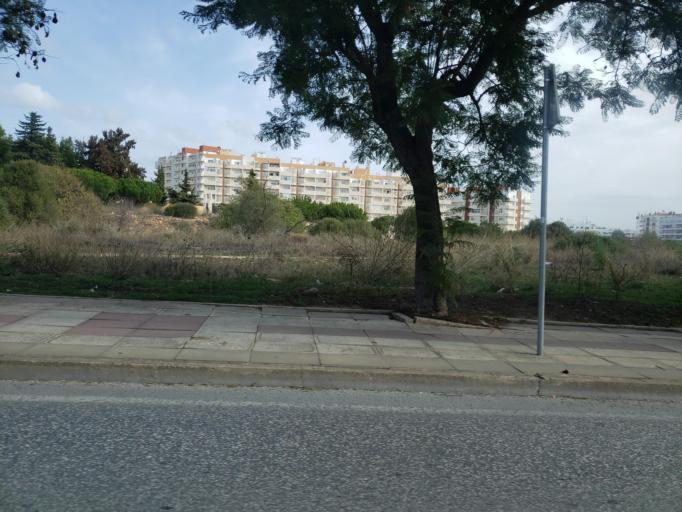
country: PT
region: Faro
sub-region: Portimao
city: Portimao
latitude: 37.1428
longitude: -8.5480
